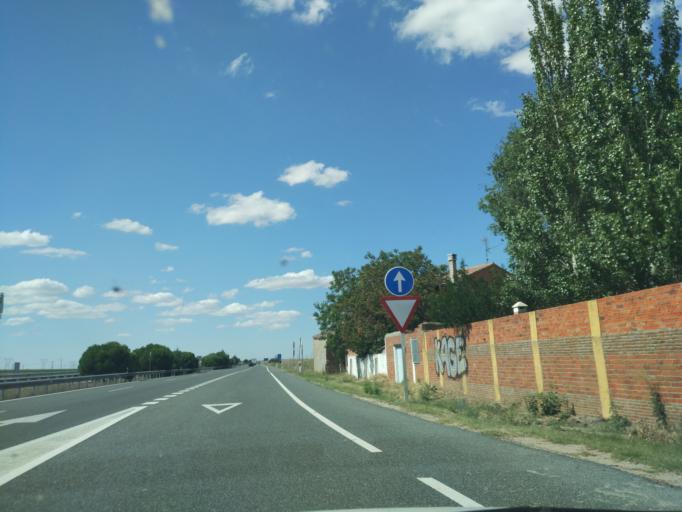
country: ES
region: Castille and Leon
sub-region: Provincia de Valladolid
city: Ataquines
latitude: 41.1827
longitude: -4.8081
